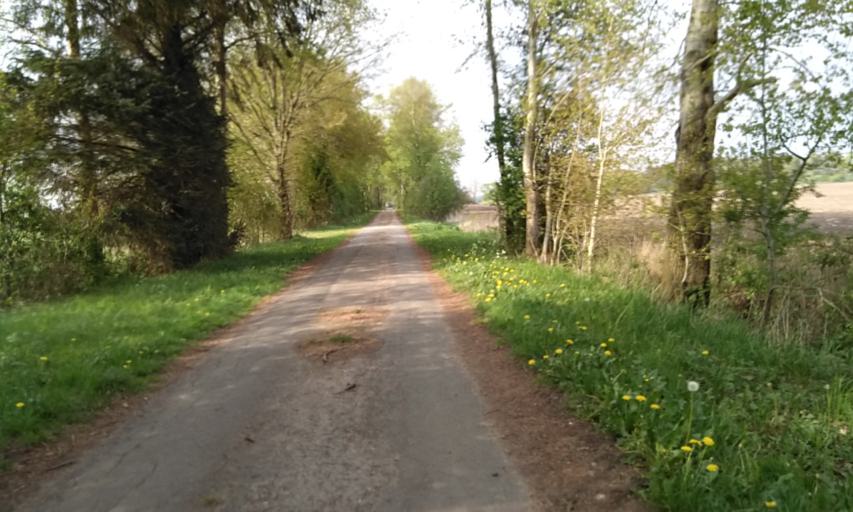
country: DE
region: Lower Saxony
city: Bliedersdorf
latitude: 53.4465
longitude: 9.5667
